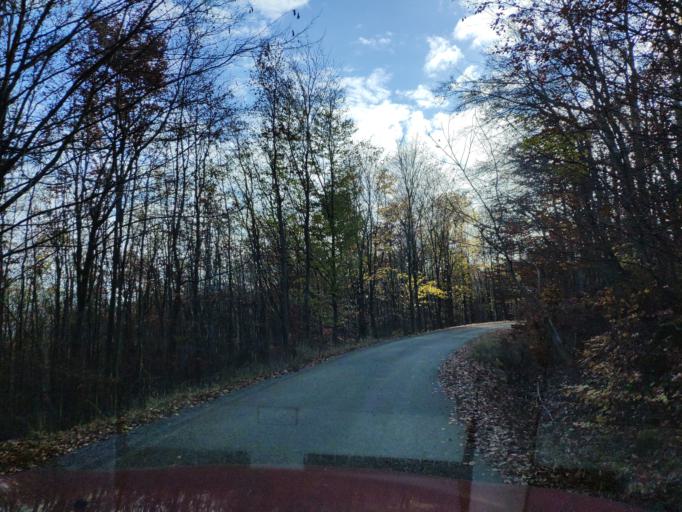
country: SK
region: Kosicky
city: Secovce
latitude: 48.6138
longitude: 21.4595
